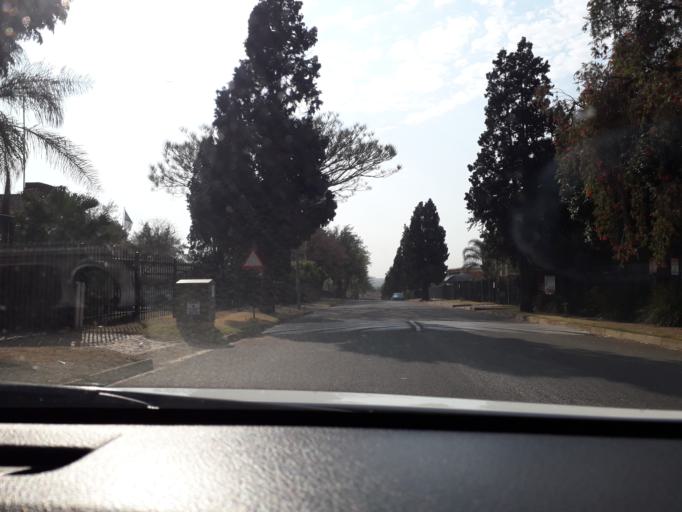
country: ZA
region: Gauteng
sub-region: Ekurhuleni Metropolitan Municipality
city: Tembisa
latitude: -26.0612
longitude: 28.2325
